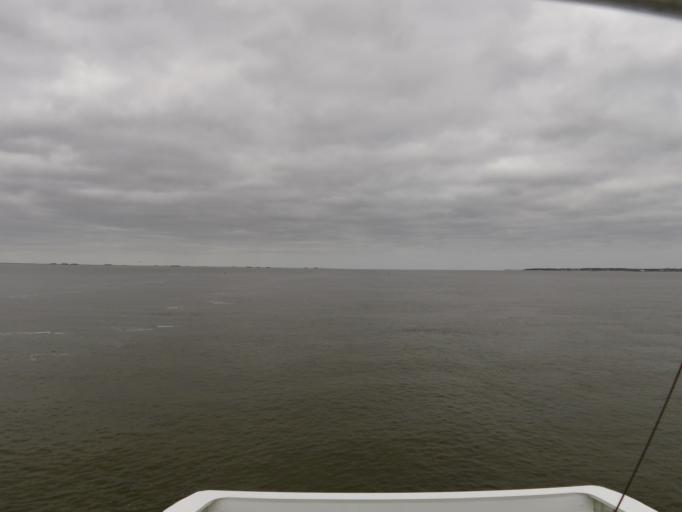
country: DE
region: Schleswig-Holstein
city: Dagebull
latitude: 54.7024
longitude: 8.6411
